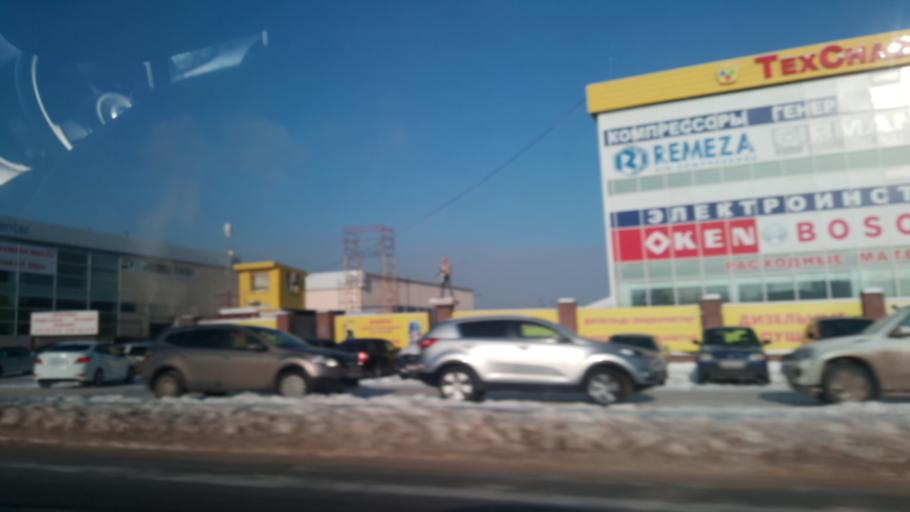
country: KZ
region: Astana Qalasy
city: Astana
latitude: 51.1761
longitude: 71.4762
